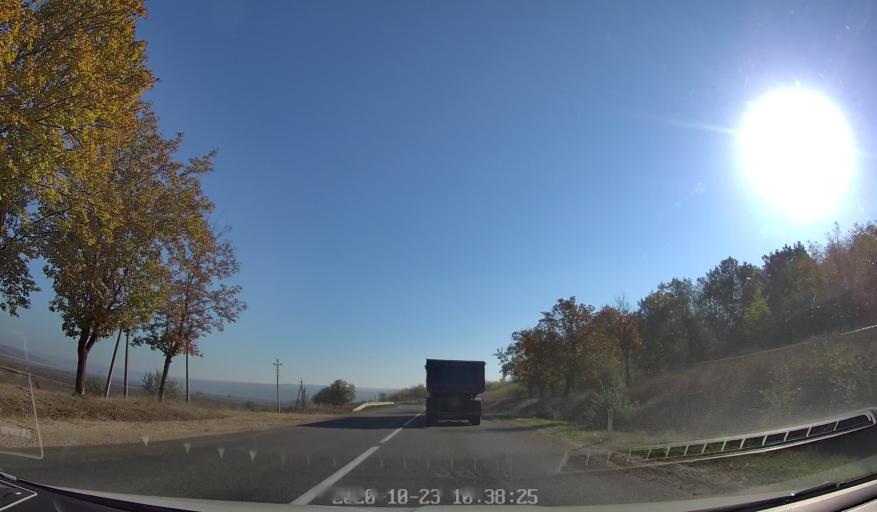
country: MD
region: Causeni
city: Causeni
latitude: 46.6674
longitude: 29.4697
